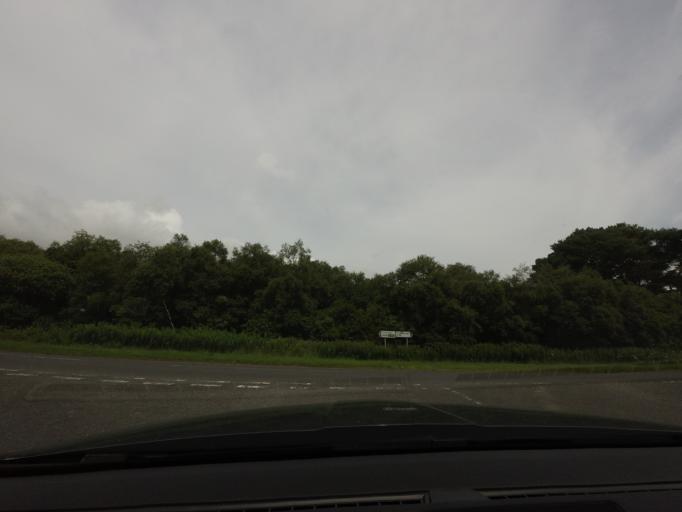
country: GB
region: Scotland
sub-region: Aberdeenshire
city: Turriff
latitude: 57.5933
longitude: -2.3029
